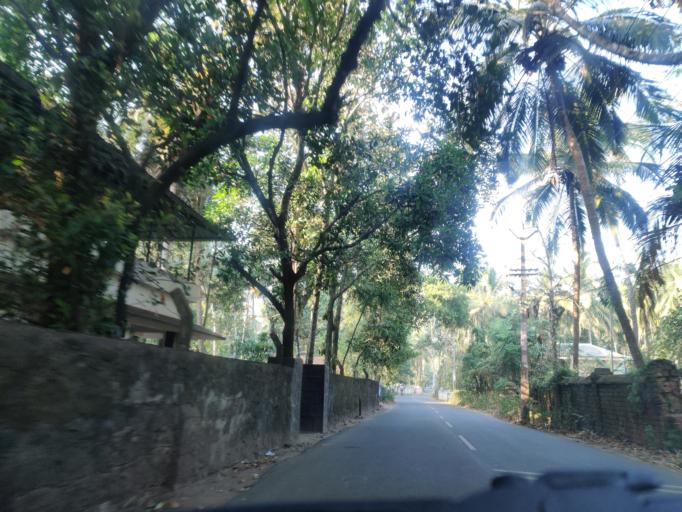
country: IN
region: Kerala
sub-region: Malappuram
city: Ponnani
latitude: 10.7293
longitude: 76.0126
